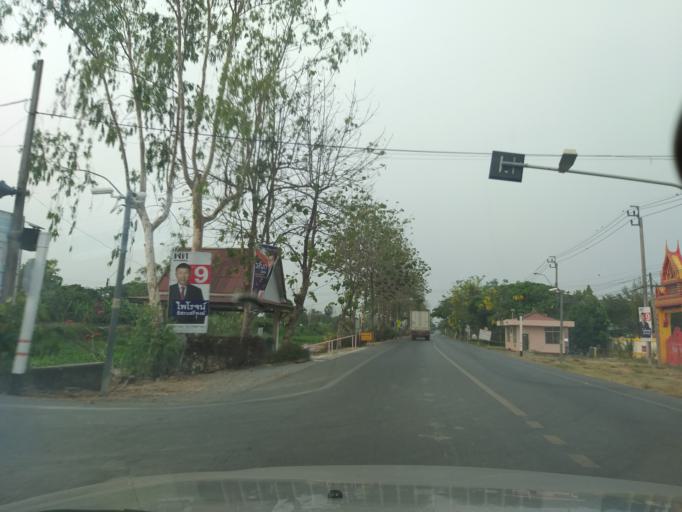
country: TH
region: Bangkok
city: Nong Chok
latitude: 13.9040
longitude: 100.8890
